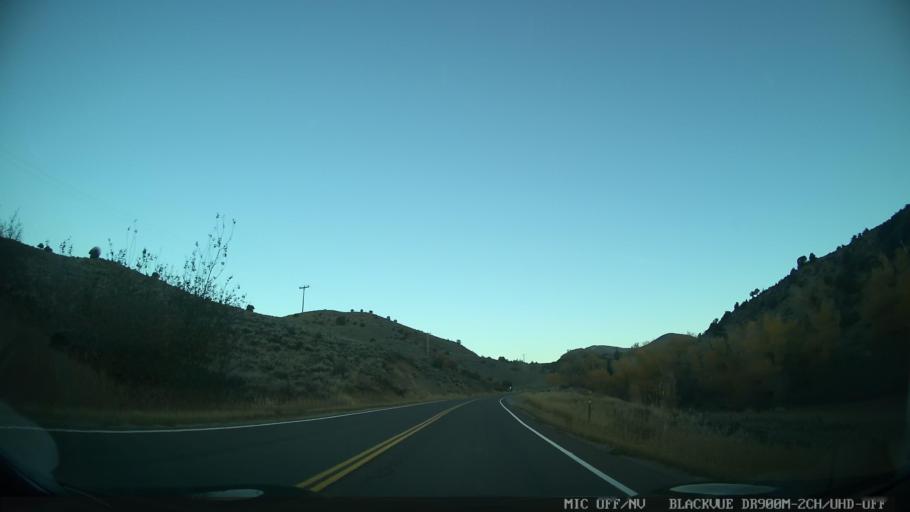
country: US
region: Colorado
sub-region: Eagle County
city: Edwards
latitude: 39.7603
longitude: -106.6748
